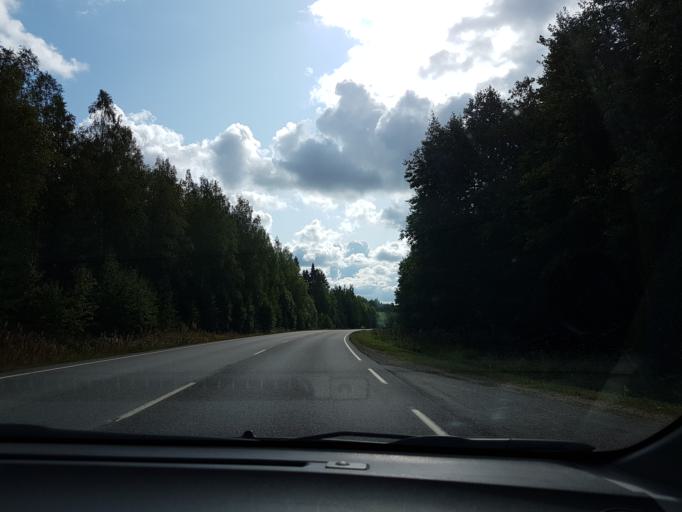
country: FI
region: Uusimaa
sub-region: Helsinki
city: Sibbo
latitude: 60.4753
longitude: 25.2270
